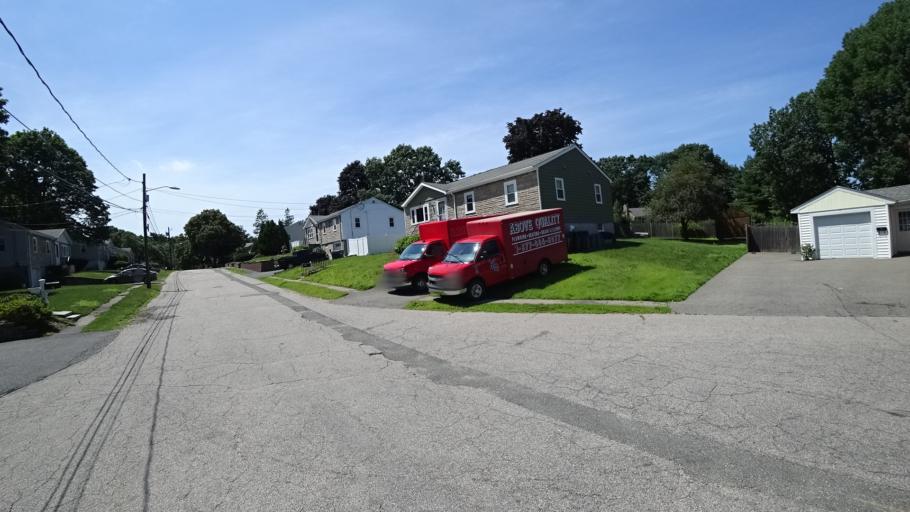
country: US
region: Massachusetts
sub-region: Norfolk County
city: Dedham
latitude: 42.2670
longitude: -71.1821
